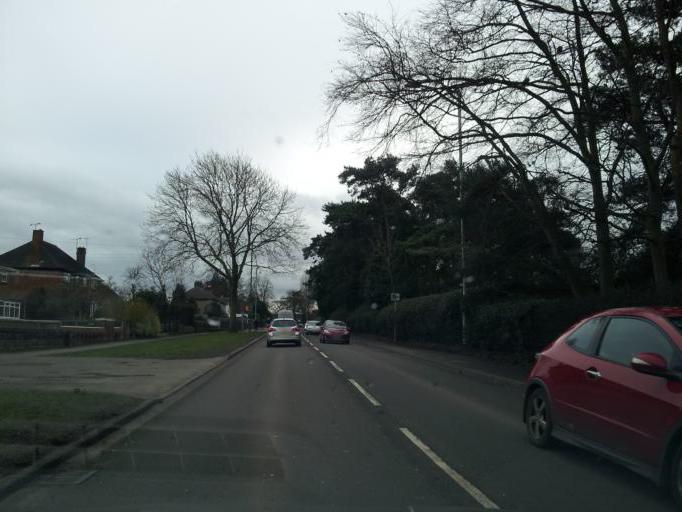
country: GB
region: England
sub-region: Staffordshire
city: Stafford
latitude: 52.7813
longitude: -2.1143
